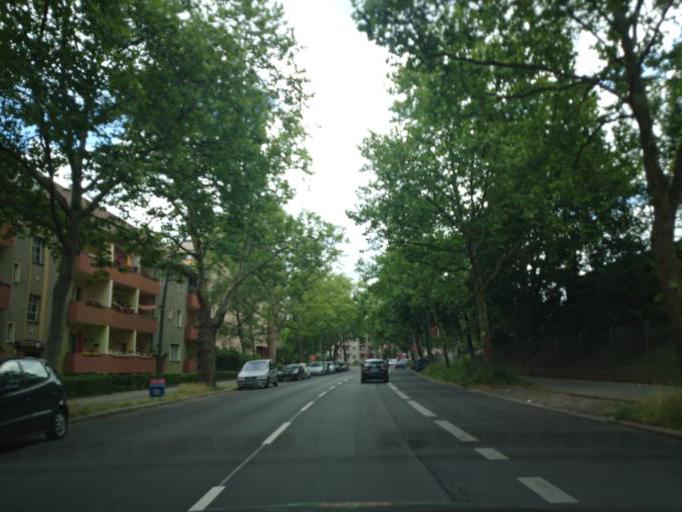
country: DE
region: Berlin
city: Mariendorf
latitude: 52.4417
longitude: 13.3795
